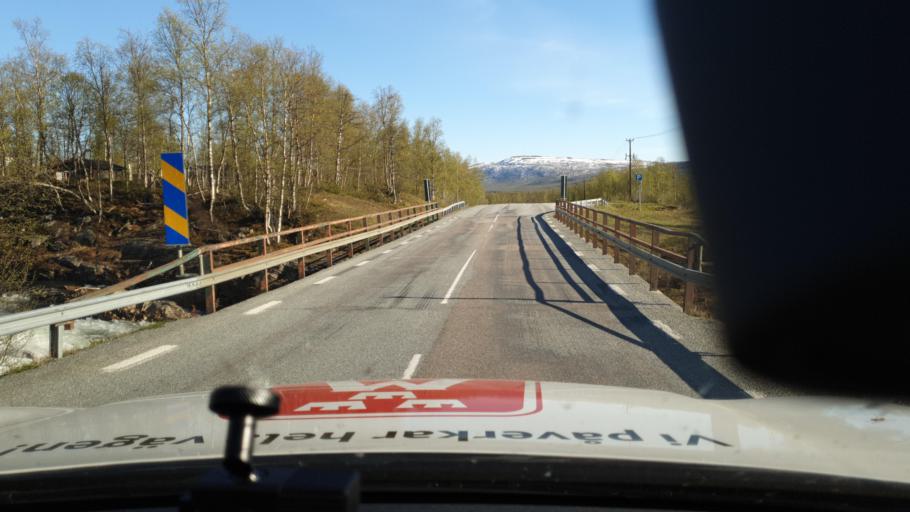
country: NO
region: Nordland
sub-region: Rana
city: Mo i Rana
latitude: 65.8434
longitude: 15.0442
